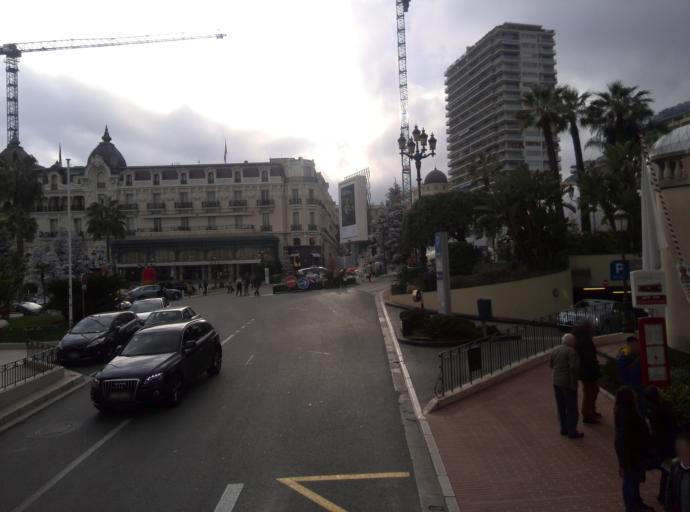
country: MC
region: Commune de Monaco
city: Monte-Carlo
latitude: 43.7400
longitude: 7.4275
